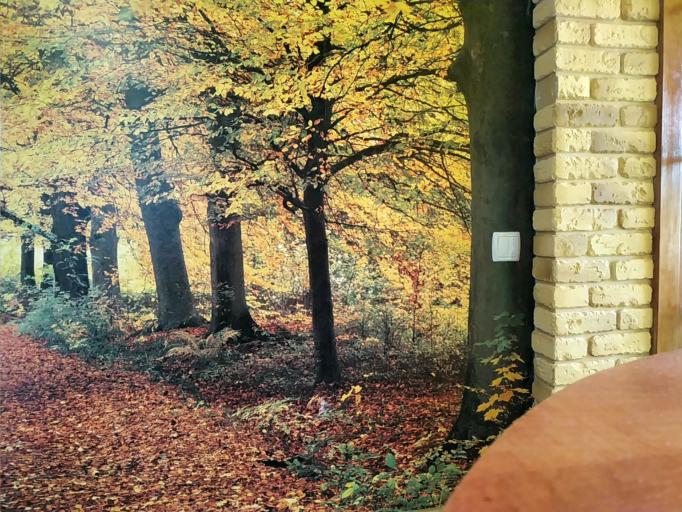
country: RU
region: Pskov
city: Dno
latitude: 57.9149
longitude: 30.1521
